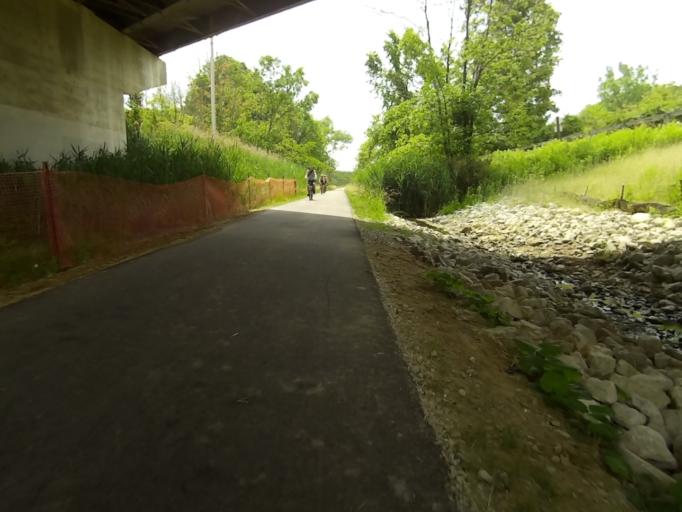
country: US
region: Ohio
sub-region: Summit County
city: Boston Heights
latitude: 41.2322
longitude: -81.4945
